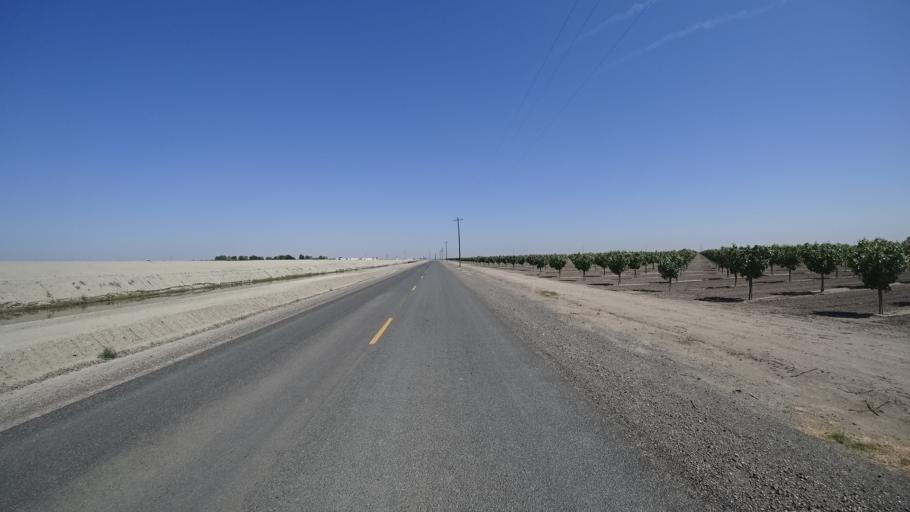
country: US
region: California
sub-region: Kings County
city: Corcoran
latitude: 36.0457
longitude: -119.5361
